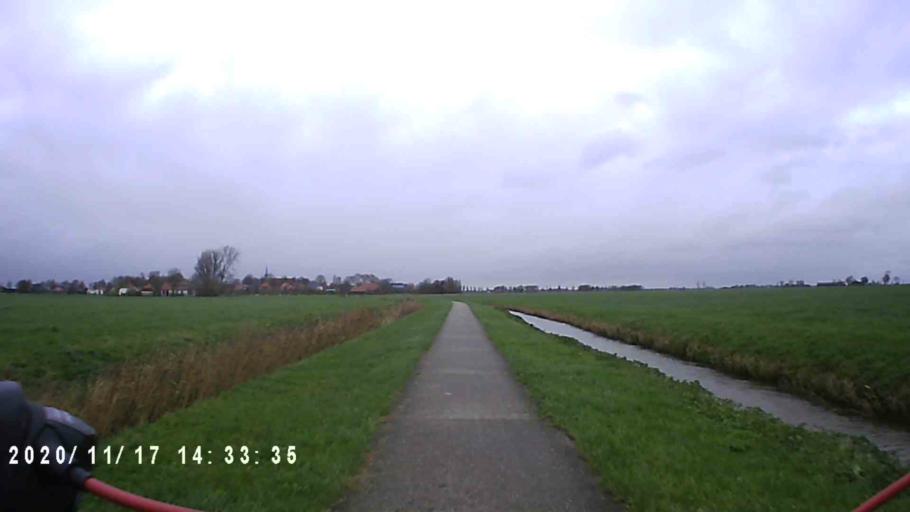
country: NL
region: Groningen
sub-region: Gemeente Zuidhorn
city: Oldehove
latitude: 53.2863
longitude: 6.3640
